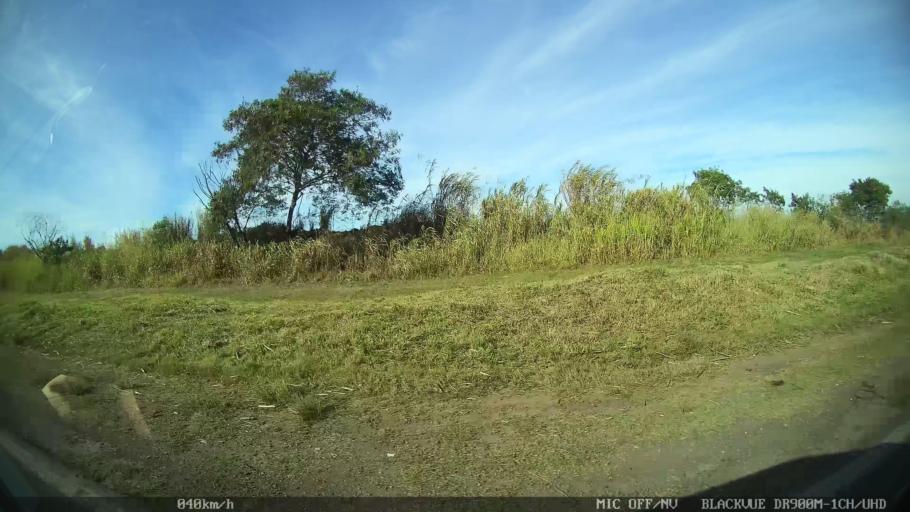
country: BR
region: Sao Paulo
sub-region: Rio Das Pedras
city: Rio das Pedras
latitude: -22.7963
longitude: -47.6005
